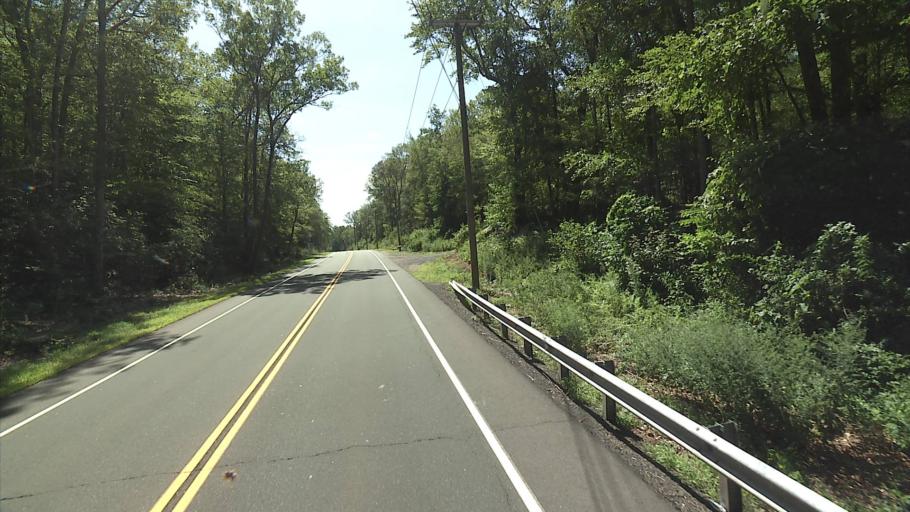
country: US
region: Connecticut
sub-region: New London County
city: Niantic
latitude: 41.3470
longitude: -72.2705
